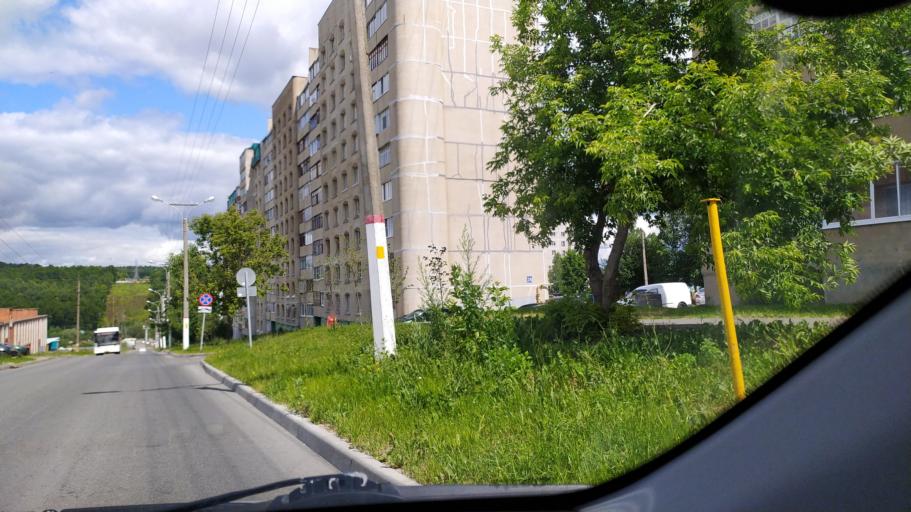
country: RU
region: Chuvashia
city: Novyye Lapsary
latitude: 56.1187
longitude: 47.1751
